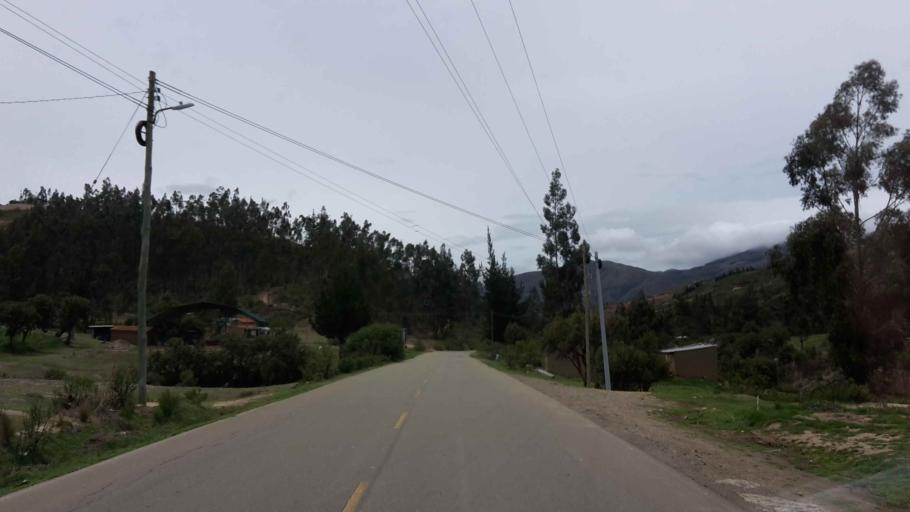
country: BO
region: Cochabamba
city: Totora
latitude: -17.6810
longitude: -65.2160
